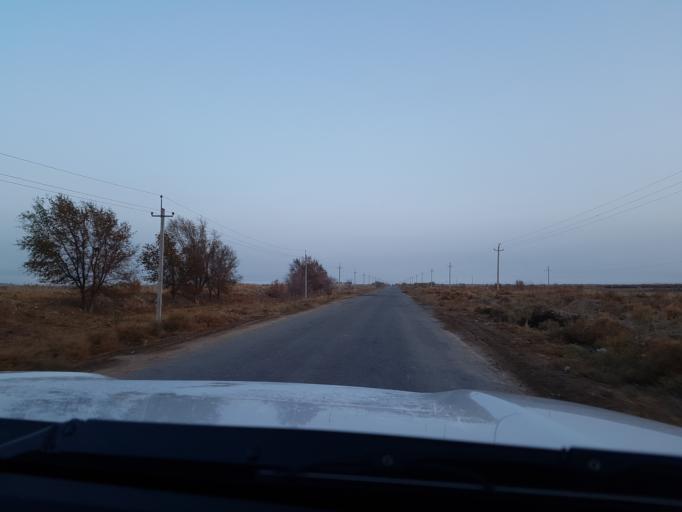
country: TM
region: Dasoguz
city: Koeneuergench
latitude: 41.7737
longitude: 58.6948
